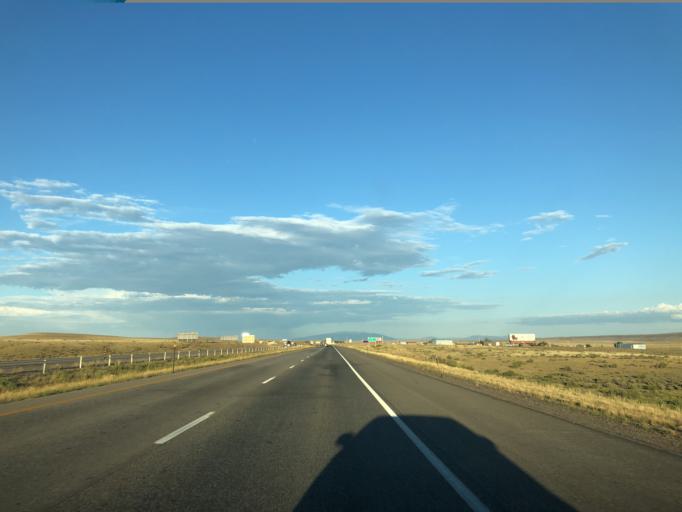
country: US
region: Wyoming
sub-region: Carbon County
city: Rawlins
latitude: 41.7860
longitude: -107.1810
